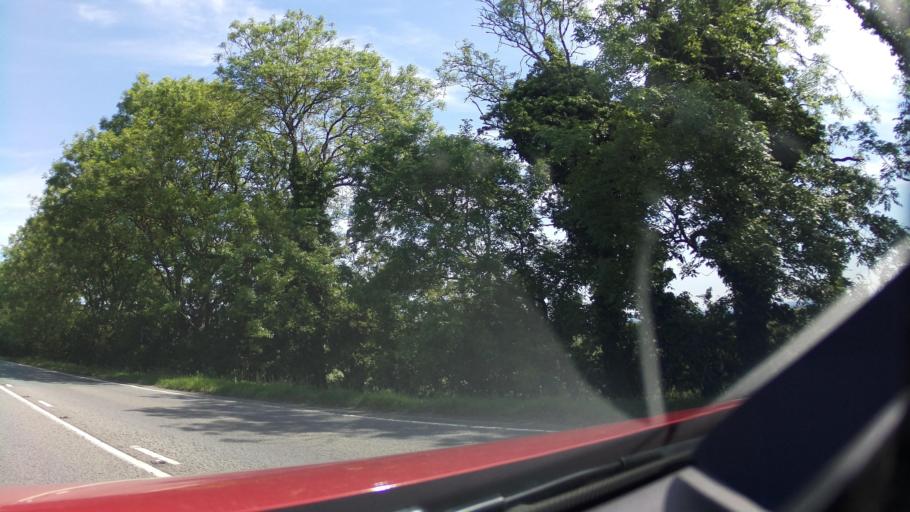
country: GB
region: England
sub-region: Lincolnshire
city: Burton
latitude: 53.3511
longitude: -0.5448
